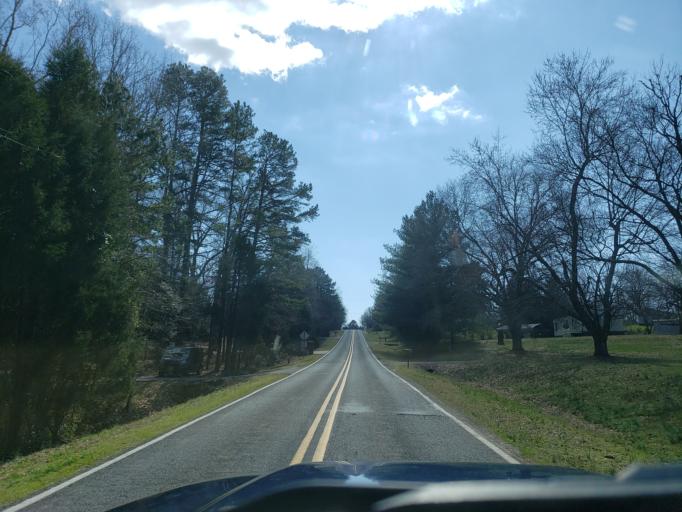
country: US
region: North Carolina
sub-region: Cleveland County
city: White Plains
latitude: 35.2248
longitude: -81.4062
